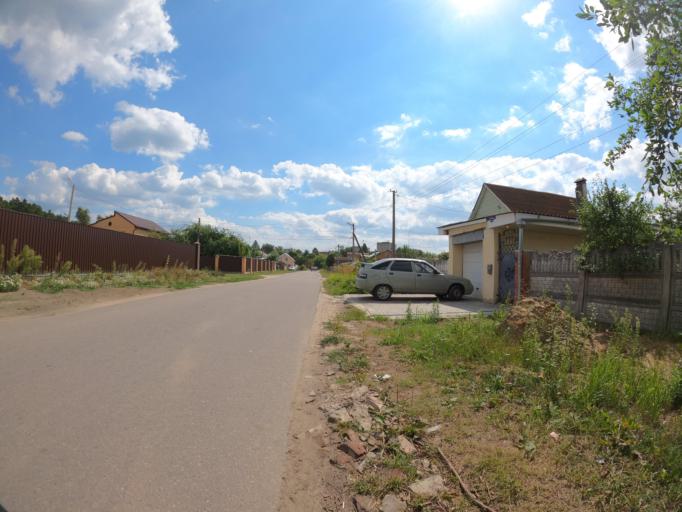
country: RU
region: Moskovskaya
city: Peski
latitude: 55.2786
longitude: 38.7484
